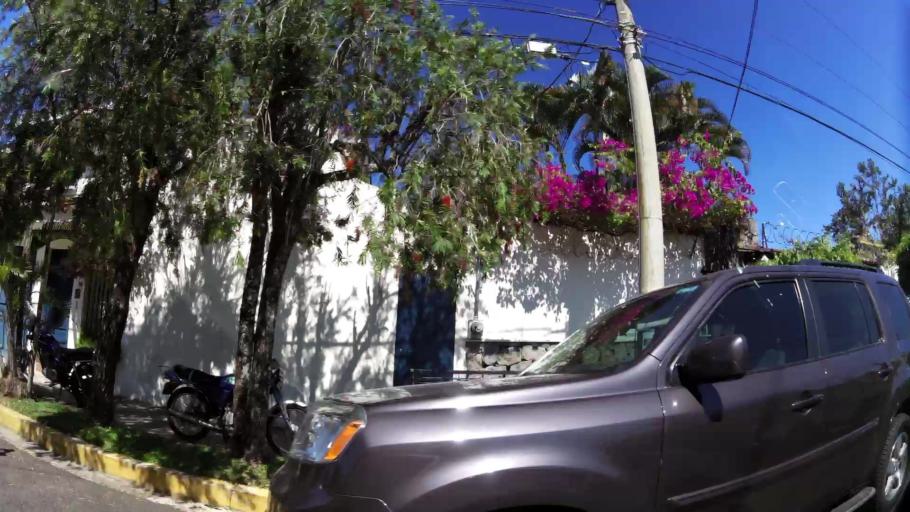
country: SV
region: La Libertad
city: Santa Tecla
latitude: 13.6673
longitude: -89.2798
